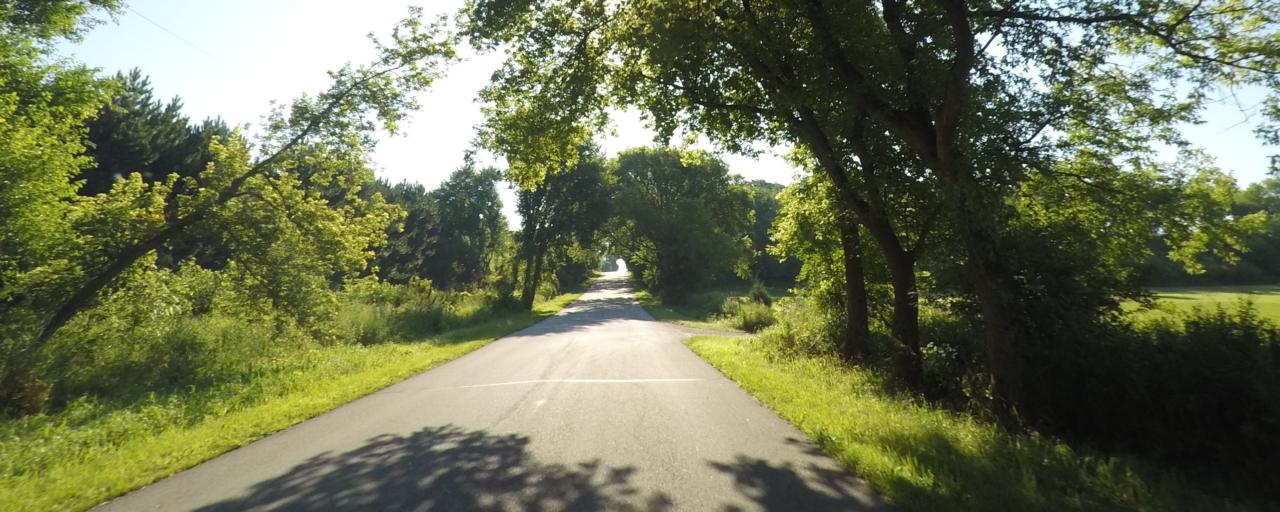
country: US
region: Wisconsin
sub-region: Jefferson County
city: Palmyra
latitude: 42.9150
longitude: -88.5831
